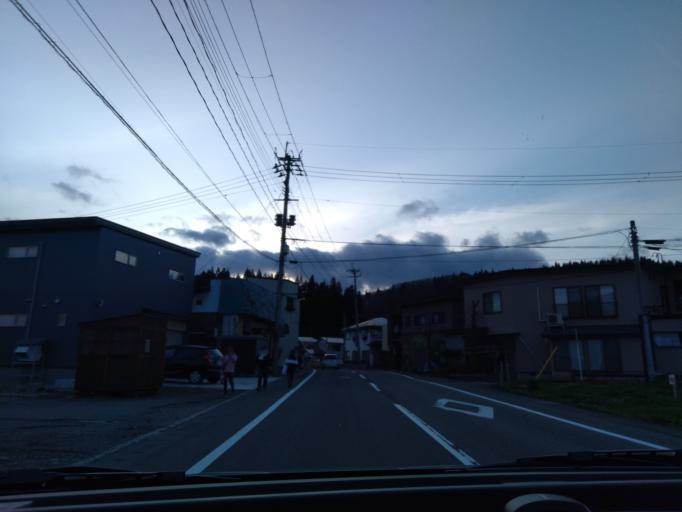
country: JP
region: Akita
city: Kakunodatemachi
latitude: 39.5950
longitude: 140.5746
